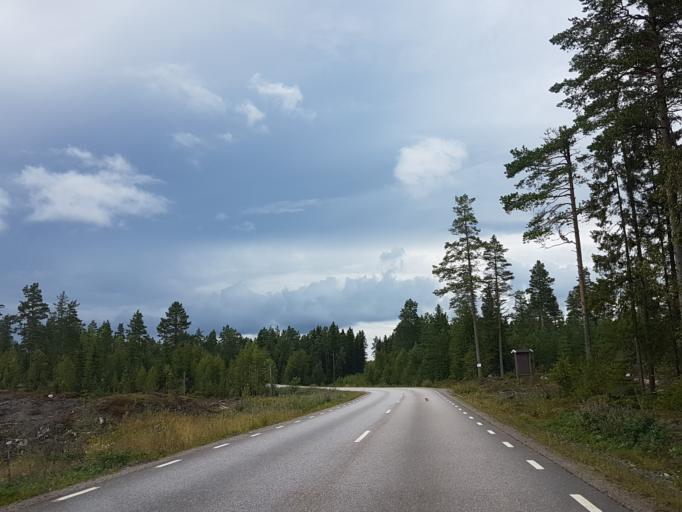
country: SE
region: Vaesterbotten
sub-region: Umea Kommun
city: Holmsund
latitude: 63.7871
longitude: 20.3844
